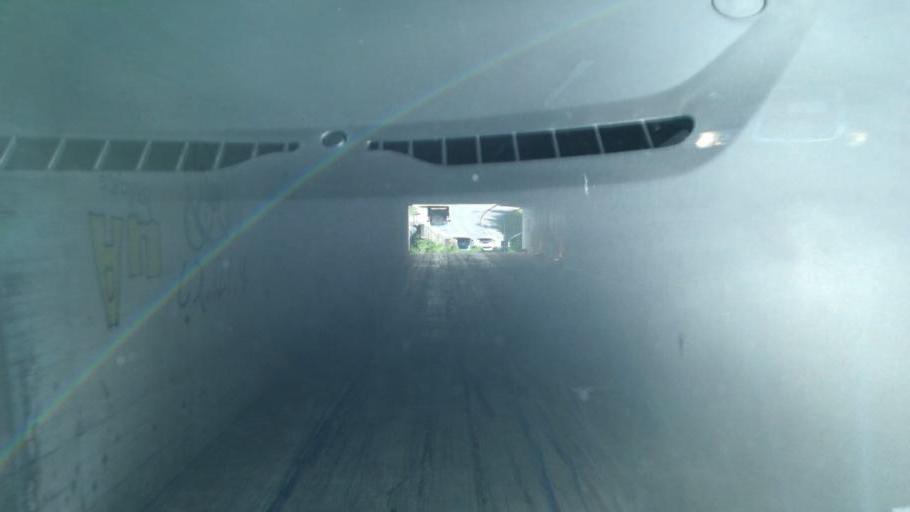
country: CH
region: Zurich
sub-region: Bezirk Buelach
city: Glattbrugg
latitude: 47.4253
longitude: 8.5586
